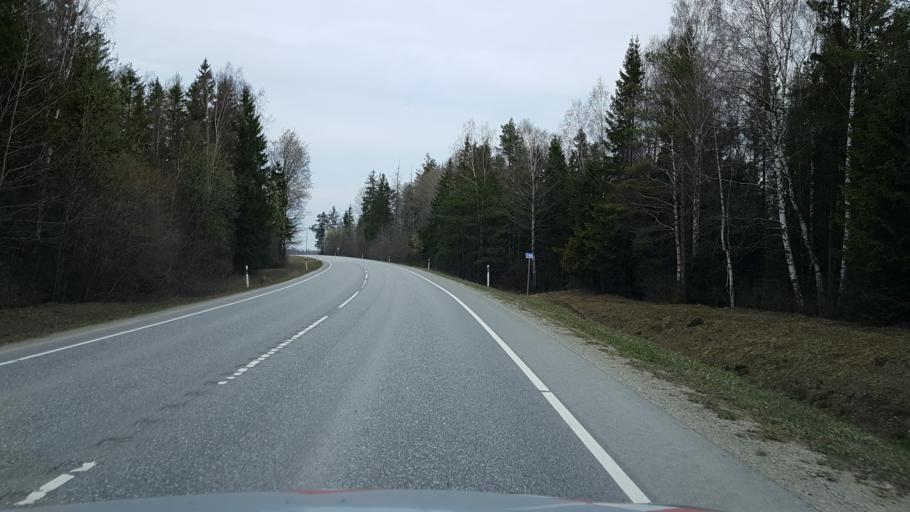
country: EE
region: Laeaene-Virumaa
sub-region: Someru vald
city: Someru
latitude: 59.3412
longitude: 26.4118
